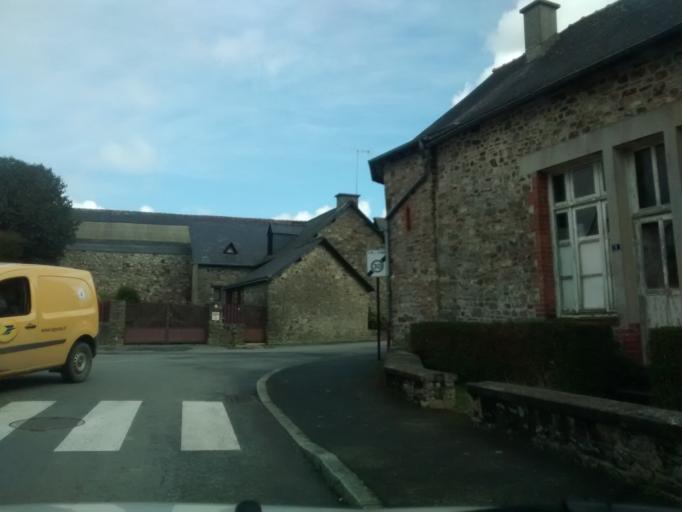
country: FR
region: Brittany
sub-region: Departement d'Ille-et-Vilaine
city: Livre-sur-Changeon
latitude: 48.2182
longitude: -1.3436
